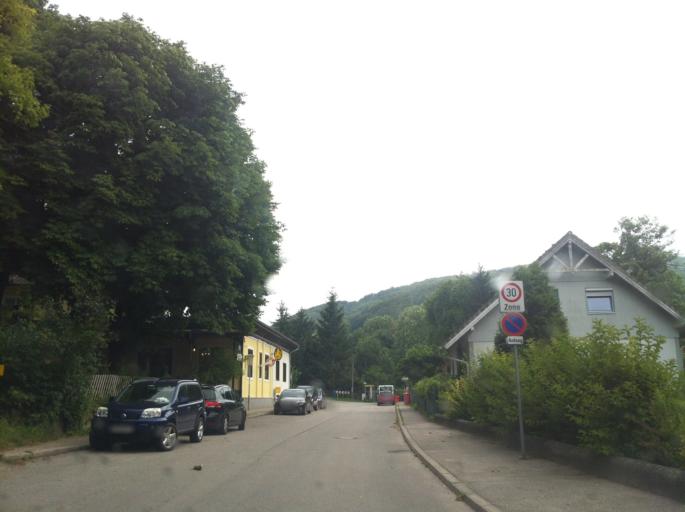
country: AT
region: Lower Austria
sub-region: Politischer Bezirk Wien-Umgebung
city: Purkersdorf
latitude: 48.1949
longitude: 16.1681
